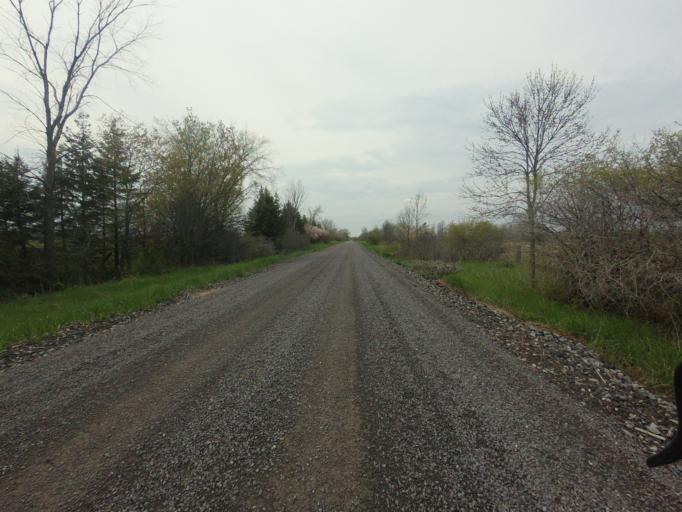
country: CA
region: Ontario
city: Carleton Place
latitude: 45.1868
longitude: -76.1599
